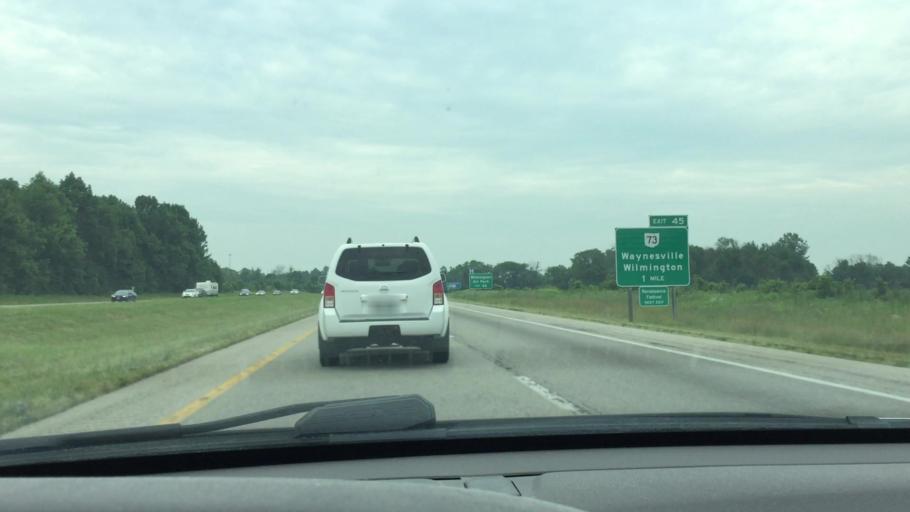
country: US
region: Ohio
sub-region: Clinton County
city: Wilmington
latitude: 39.4776
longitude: -83.9605
